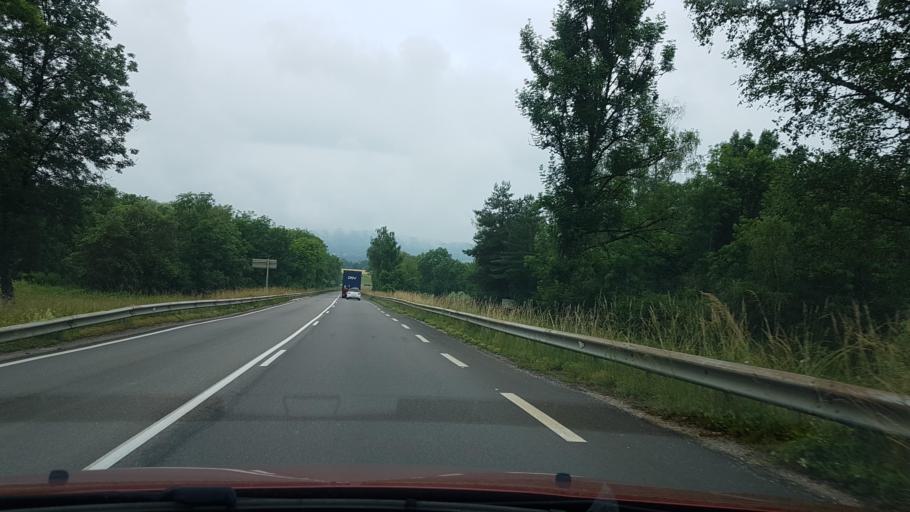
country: FR
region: Franche-Comte
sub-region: Departement du Jura
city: Clairvaux-les-Lacs
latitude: 46.5876
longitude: 5.7373
